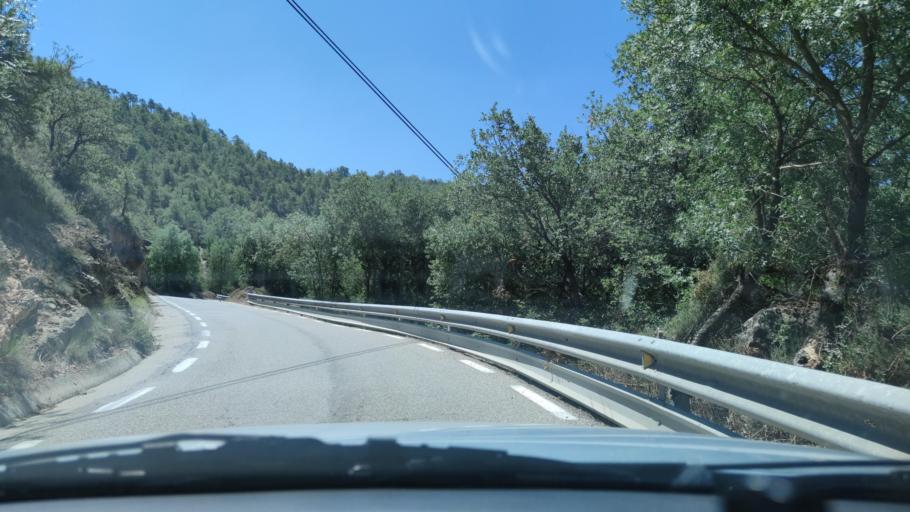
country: ES
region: Catalonia
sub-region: Provincia de Lleida
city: Tora de Riubregos
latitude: 41.8189
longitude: 1.4152
